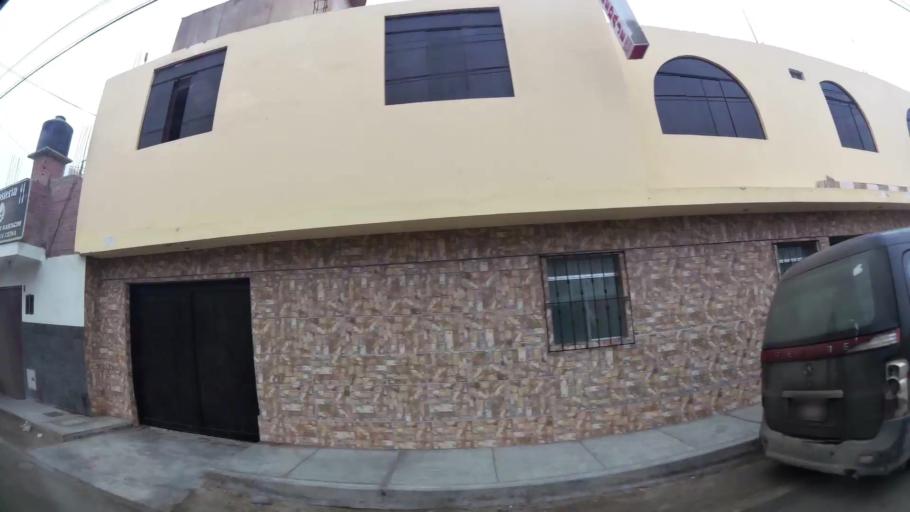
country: PE
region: Ica
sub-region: Provincia de Pisco
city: Pisco
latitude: -13.7341
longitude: -76.2228
